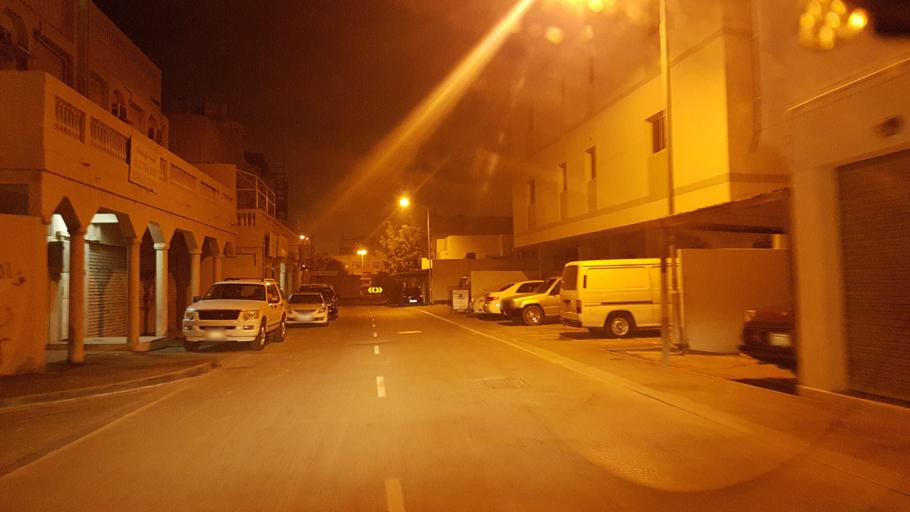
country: BH
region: Manama
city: Jidd Hafs
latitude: 26.2220
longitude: 50.5404
